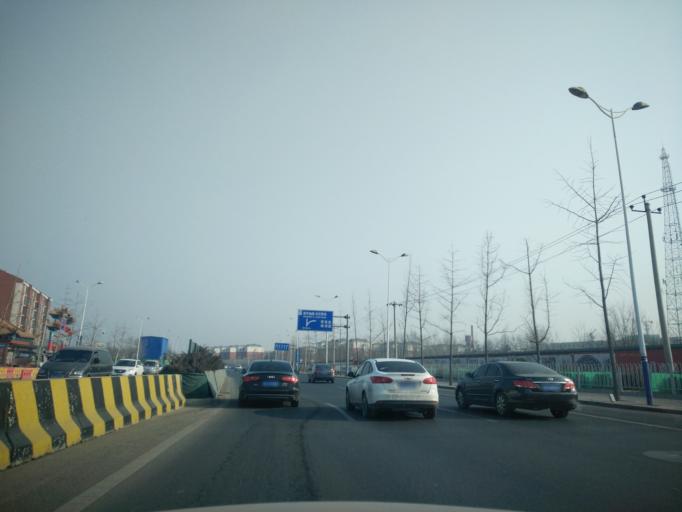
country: CN
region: Beijing
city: Xingfeng
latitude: 39.7398
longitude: 116.3595
